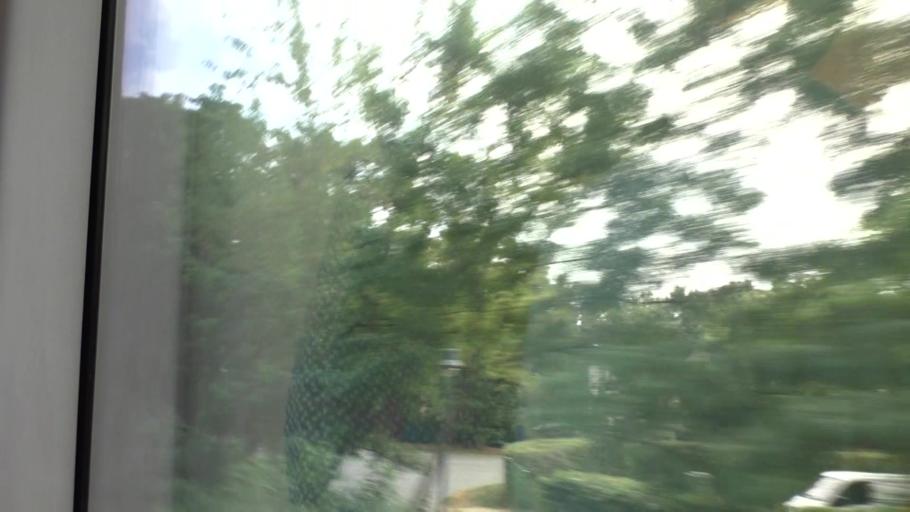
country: DE
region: Brandenburg
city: Konigs Wusterhausen
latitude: 52.2998
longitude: 13.6635
